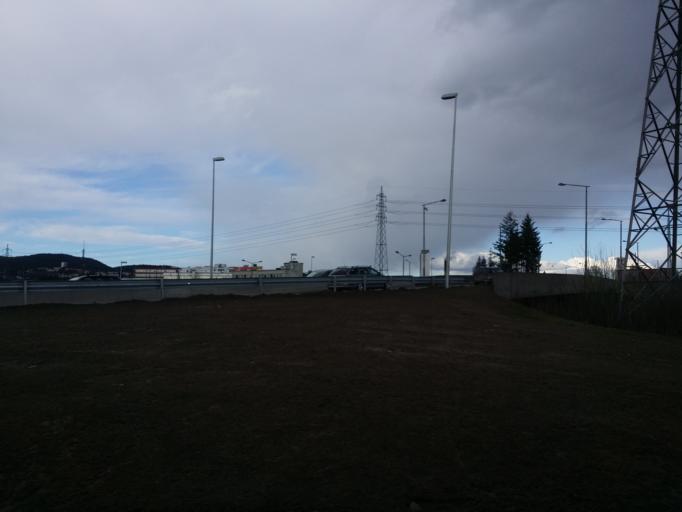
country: NO
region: Oslo
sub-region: Oslo
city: Oslo
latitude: 59.9223
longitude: 10.8063
